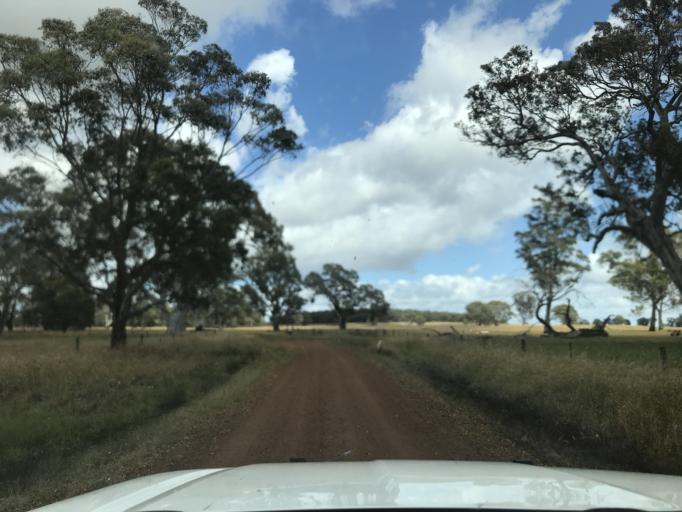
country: AU
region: South Australia
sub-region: Wattle Range
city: Penola
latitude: -37.1826
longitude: 141.4419
